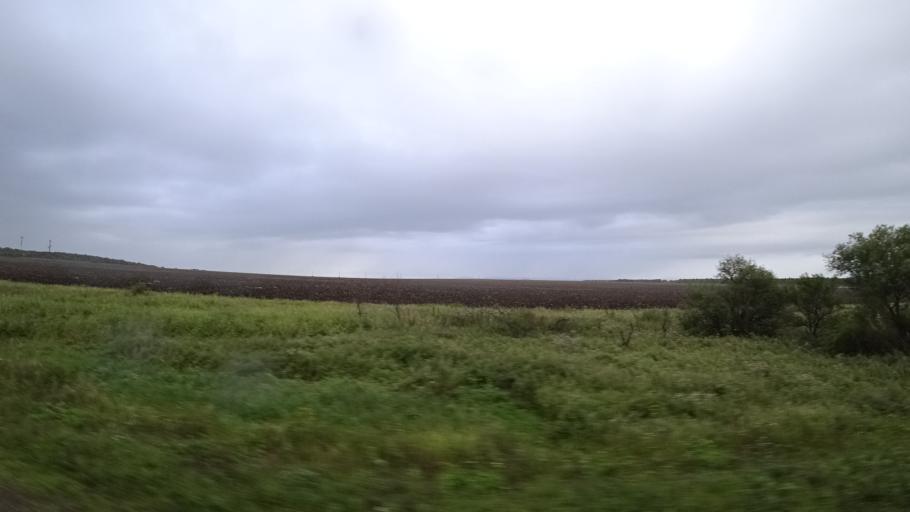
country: RU
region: Primorskiy
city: Chernigovka
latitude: 44.3642
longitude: 132.5437
